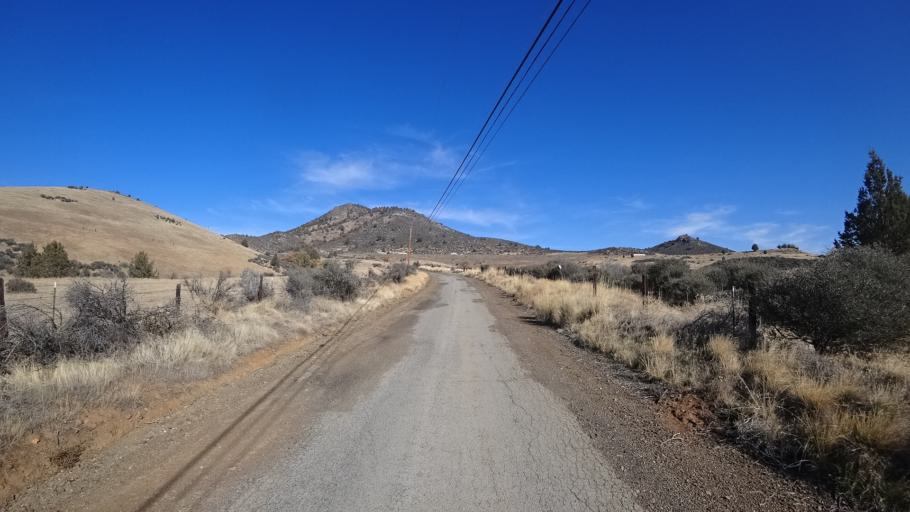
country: US
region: California
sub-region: Siskiyou County
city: Yreka
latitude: 41.7775
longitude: -122.5893
